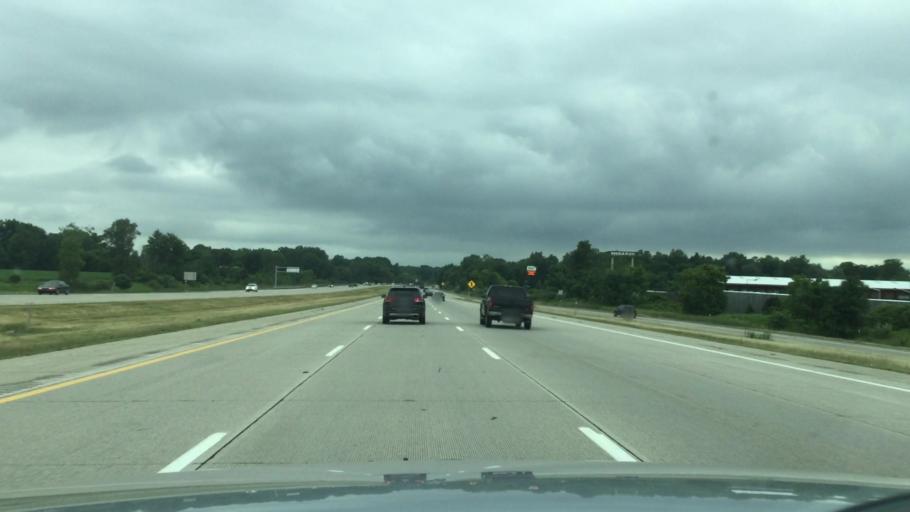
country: US
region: Michigan
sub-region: Genesee County
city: Davison
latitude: 43.0167
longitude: -83.5587
